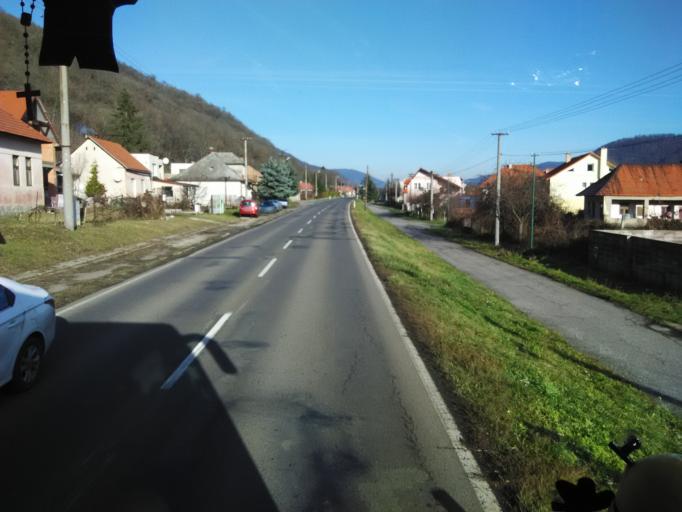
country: SK
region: Nitriansky
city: Tlmace
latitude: 48.3502
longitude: 18.5654
